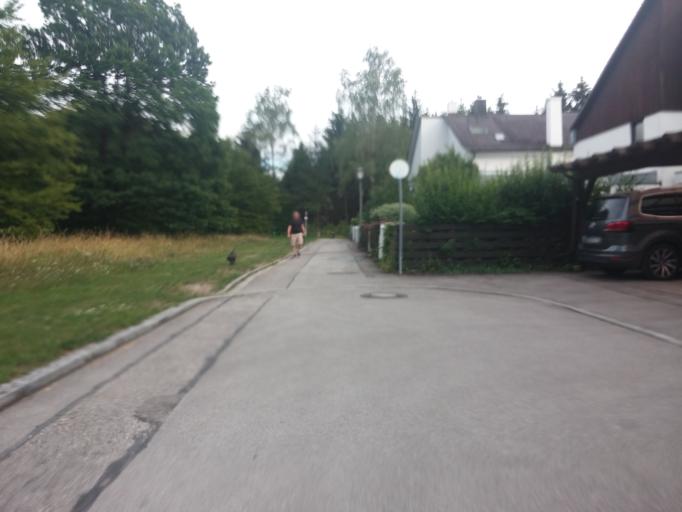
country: DE
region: Bavaria
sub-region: Upper Bavaria
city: Haar
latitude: 48.1018
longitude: 11.7054
